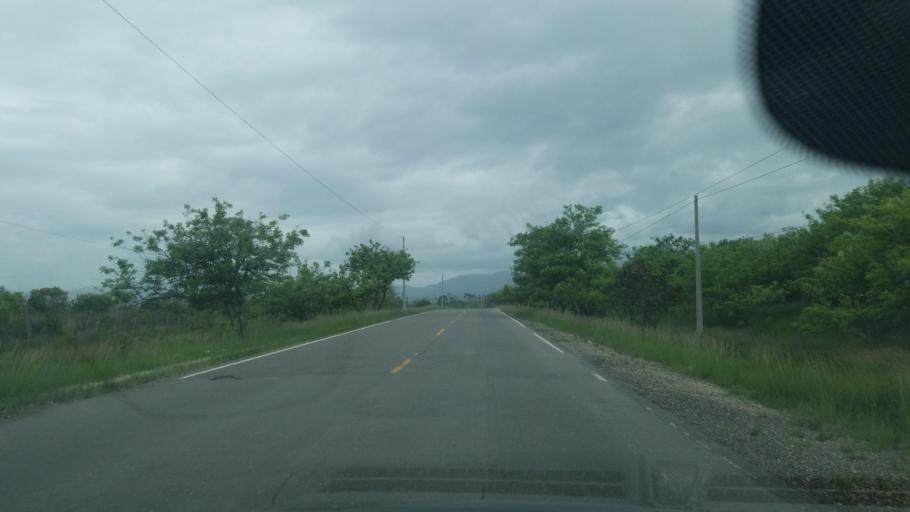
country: HN
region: Ocotepeque
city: Lucerna
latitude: 14.5319
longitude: -88.9503
